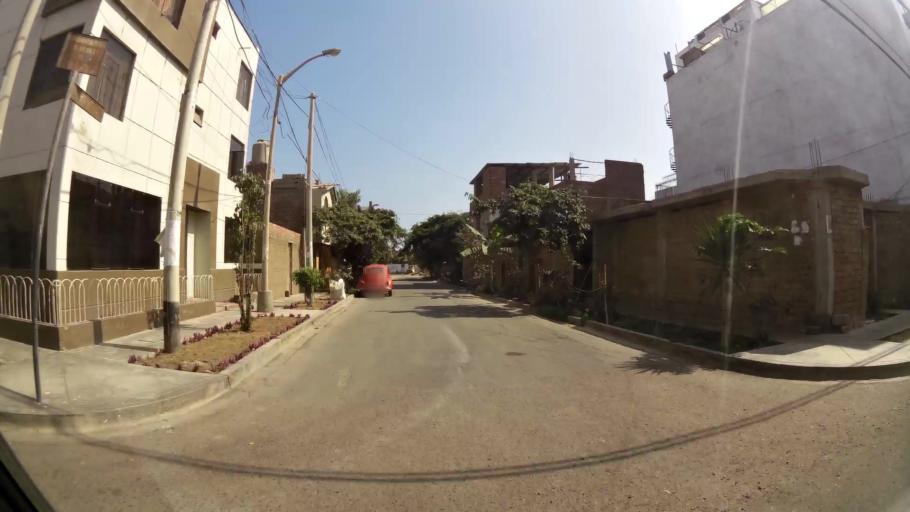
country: PE
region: La Libertad
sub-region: Provincia de Trujillo
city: Trujillo
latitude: -8.1236
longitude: -79.0424
